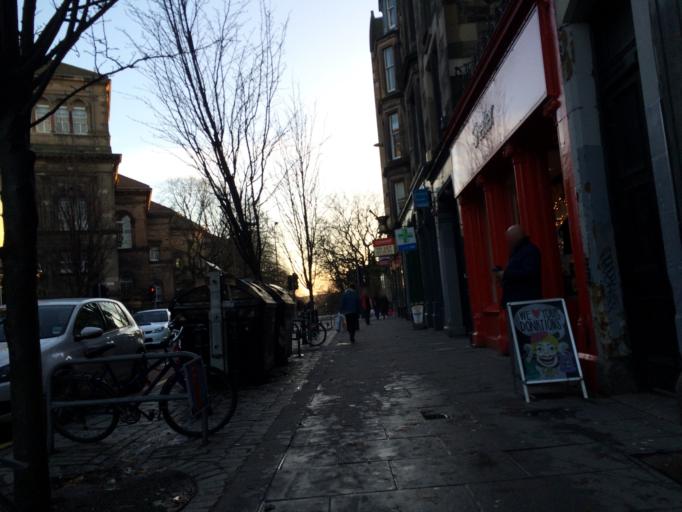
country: GB
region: Scotland
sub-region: Edinburgh
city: Edinburgh
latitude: 55.9458
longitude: -3.1911
